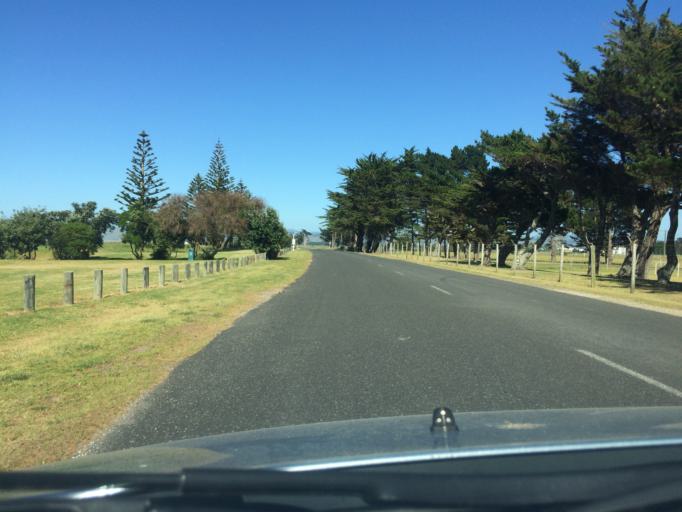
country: NZ
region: Gisborne
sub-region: Gisborne District
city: Gisborne
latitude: -38.6727
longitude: 177.9943
